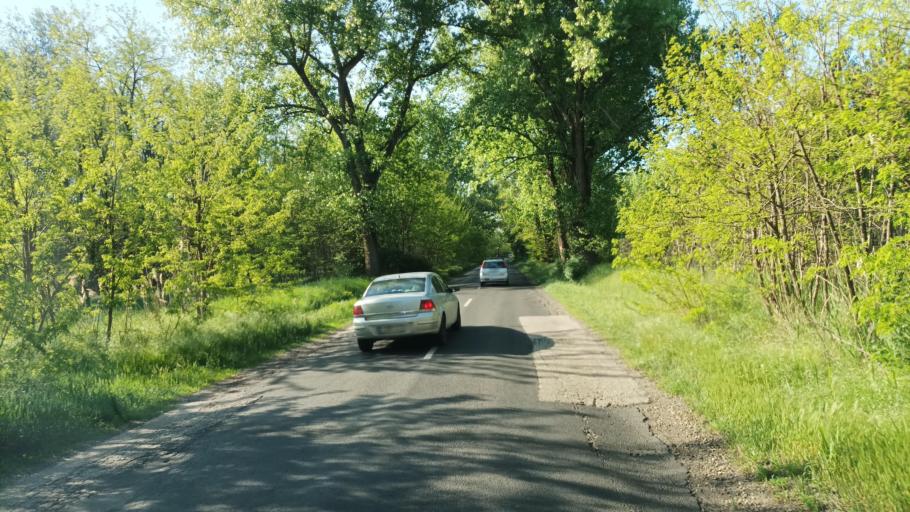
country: HU
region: Pest
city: Monor
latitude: 47.3168
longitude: 19.4440
